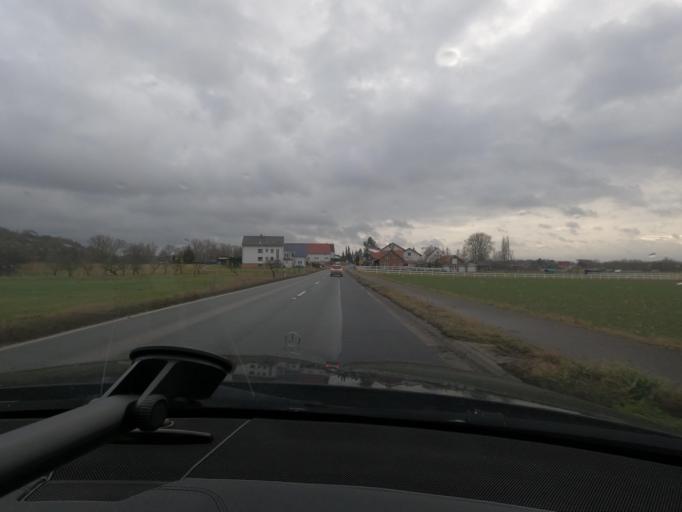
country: DE
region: Hesse
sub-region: Regierungsbezirk Kassel
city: Volkmarsen
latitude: 51.4197
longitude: 9.1232
